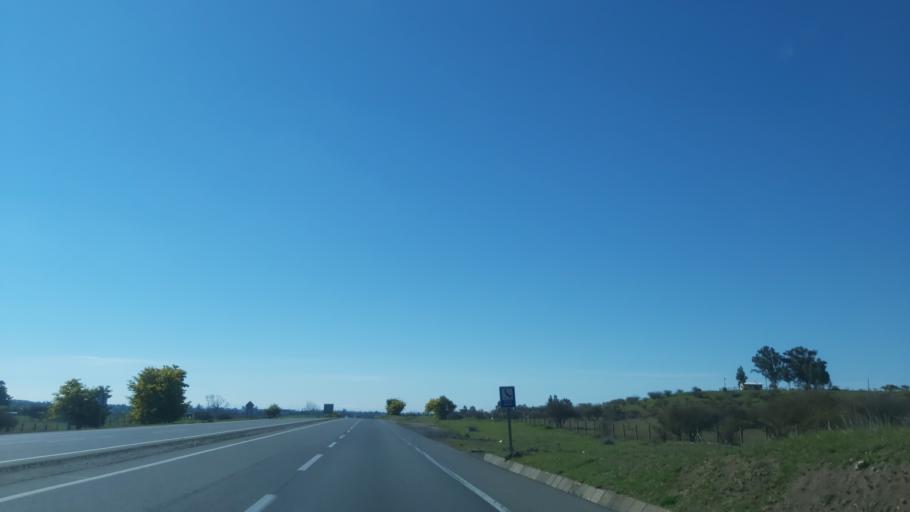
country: CL
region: Biobio
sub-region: Provincia de Nuble
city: Bulnes
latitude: -36.6601
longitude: -72.2558
